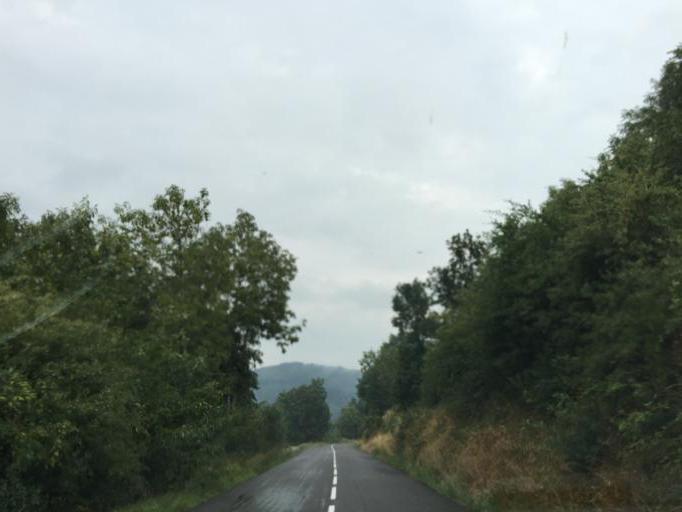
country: FR
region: Rhone-Alpes
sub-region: Departement de la Loire
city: Saint-Christo-en-Jarez
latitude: 45.5313
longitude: 4.4916
